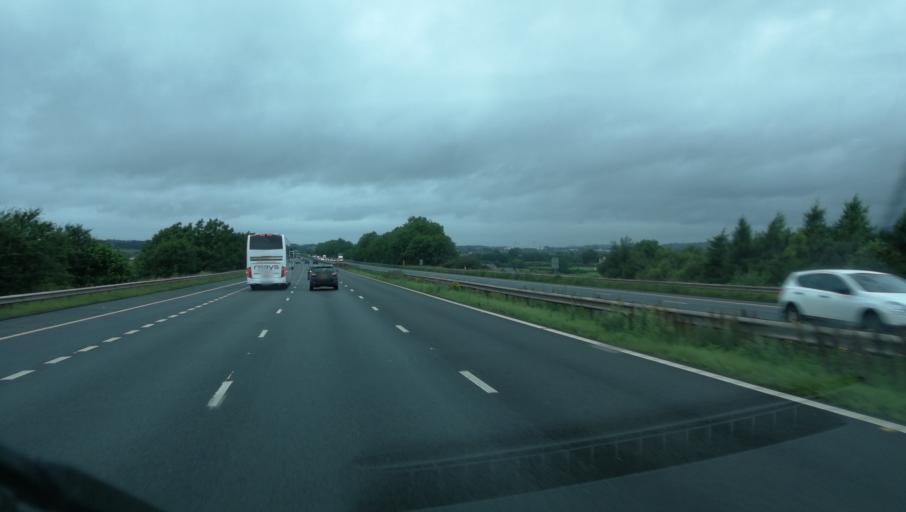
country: GB
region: England
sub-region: Borough of Bolton
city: Westhoughton
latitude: 53.5580
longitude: -2.4972
